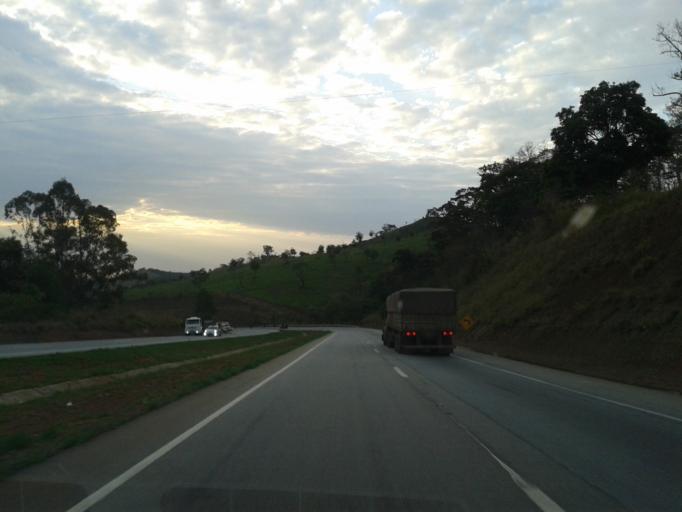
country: BR
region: Minas Gerais
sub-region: Mateus Leme
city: Mateus Leme
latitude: -19.9220
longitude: -44.4670
